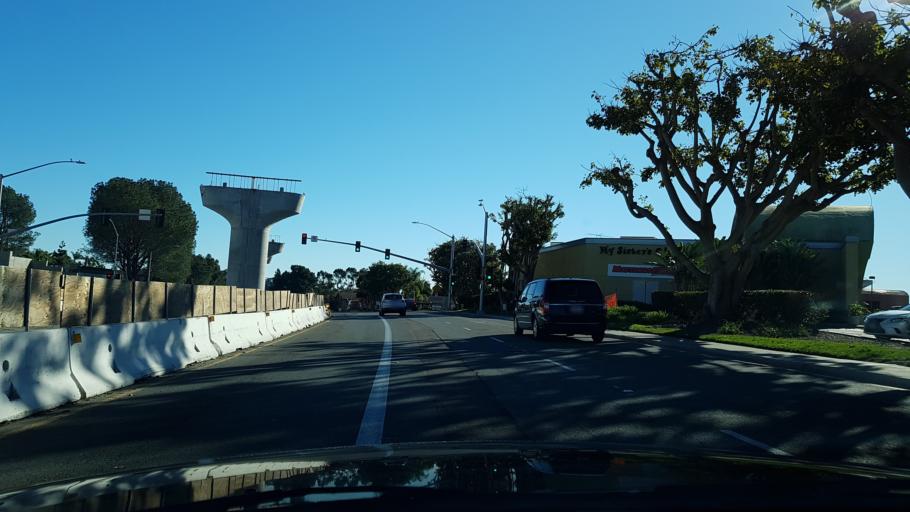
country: US
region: California
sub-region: San Diego County
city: La Jolla
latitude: 32.8689
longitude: -117.2142
